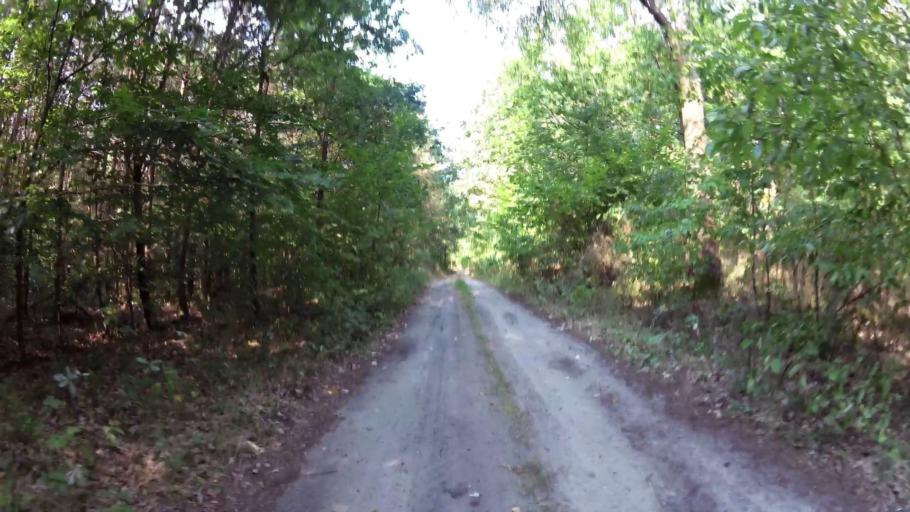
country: PL
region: West Pomeranian Voivodeship
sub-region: Powiat gryfinski
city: Moryn
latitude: 52.8760
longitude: 14.4289
